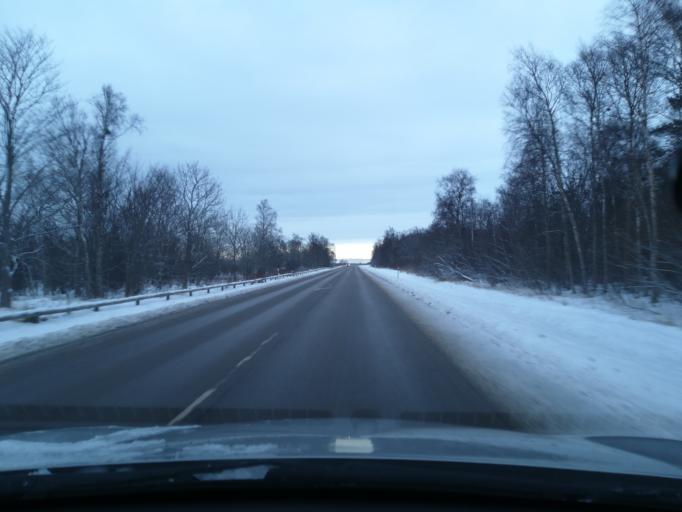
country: EE
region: Harju
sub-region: Keila linn
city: Keila
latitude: 59.4171
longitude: 24.3154
